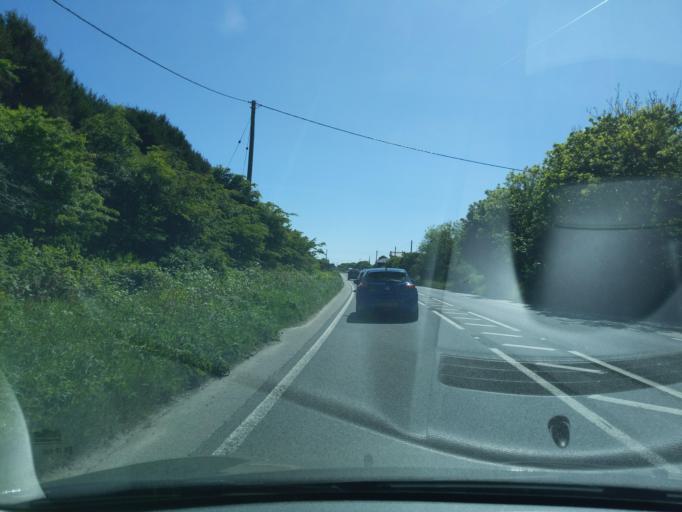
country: GB
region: England
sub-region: Cornwall
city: Wendron
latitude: 50.1563
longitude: -5.1895
